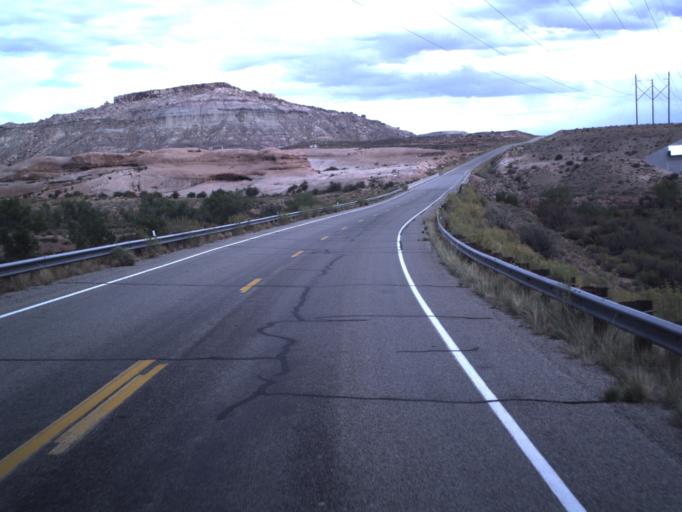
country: US
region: Utah
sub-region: San Juan County
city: Blanding
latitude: 37.2998
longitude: -109.4597
